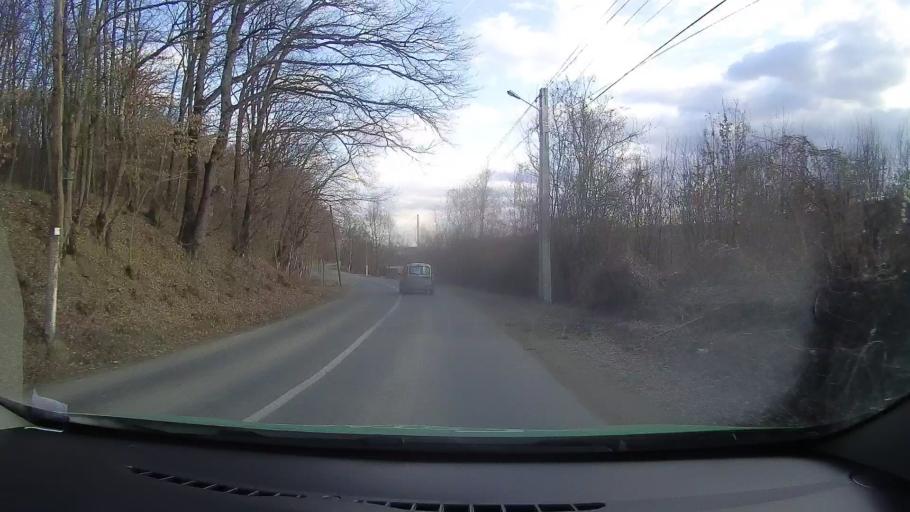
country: RO
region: Dambovita
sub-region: Comuna Gura Ocnitei
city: Gura Ocnitei
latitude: 44.9560
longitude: 25.5523
